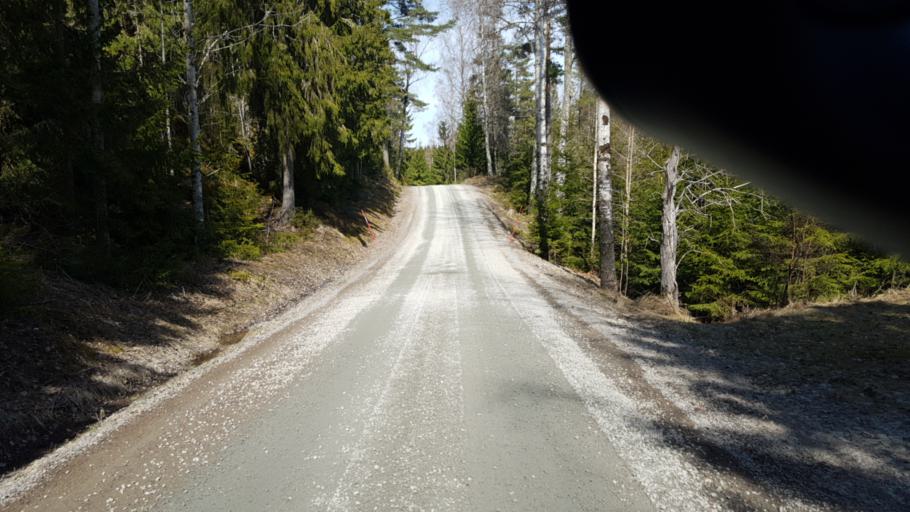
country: SE
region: Vaermland
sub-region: Grums Kommun
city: Slottsbron
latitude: 59.4614
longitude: 12.9188
